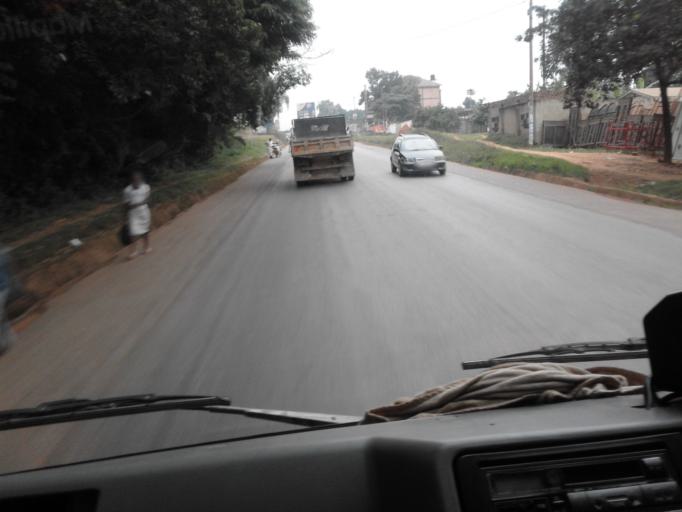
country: UG
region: Central Region
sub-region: Wakiso District
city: Bweyogerere
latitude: 0.3670
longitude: 32.7074
